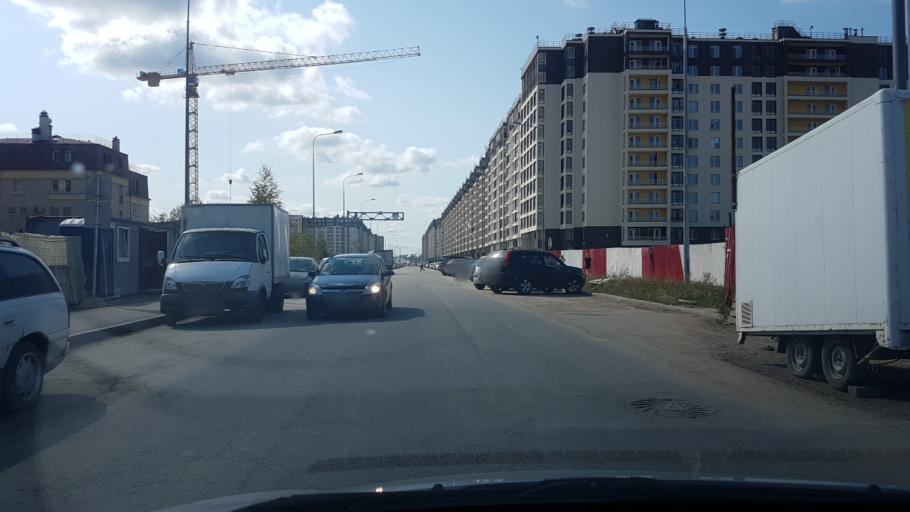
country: RU
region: St.-Petersburg
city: Sosnovaya Polyana
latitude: 59.8446
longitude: 30.1143
